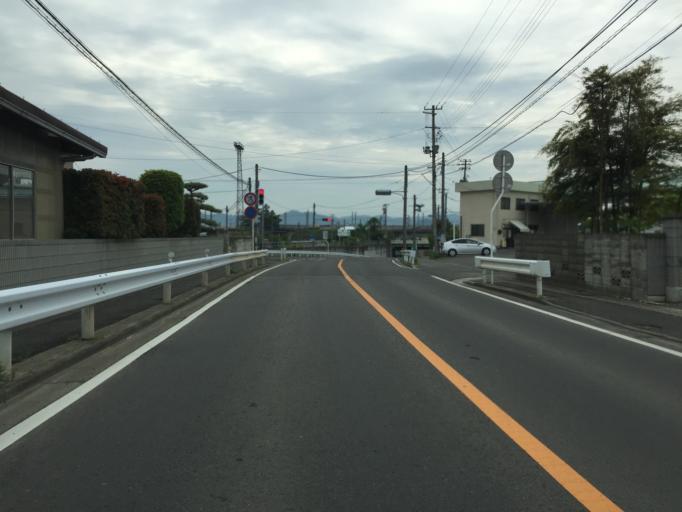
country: JP
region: Fukushima
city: Fukushima-shi
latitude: 37.7925
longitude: 140.4686
